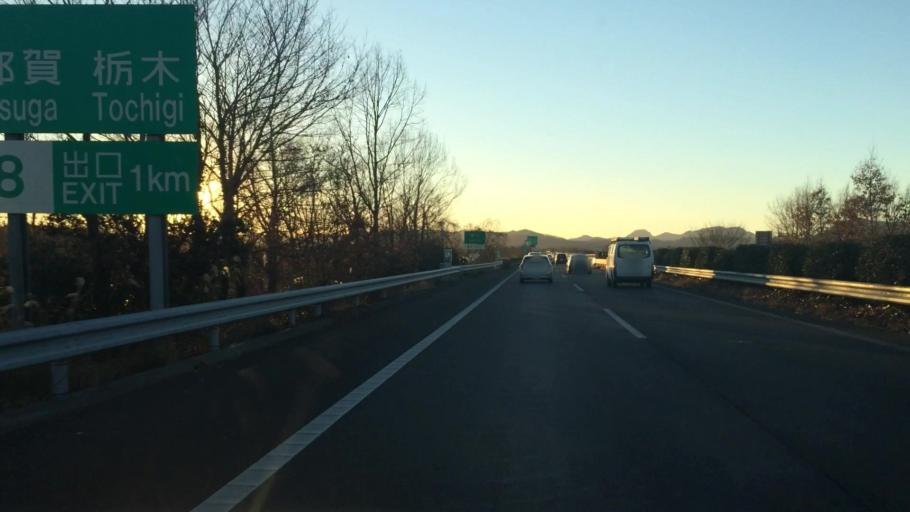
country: JP
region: Tochigi
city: Mibu
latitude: 36.4413
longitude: 139.7694
